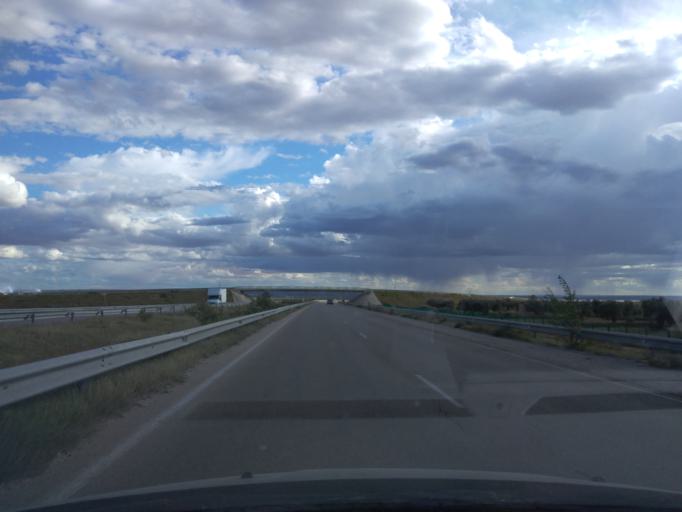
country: TN
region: Al Munastir
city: Manzil Kamil
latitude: 35.5224
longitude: 10.6264
